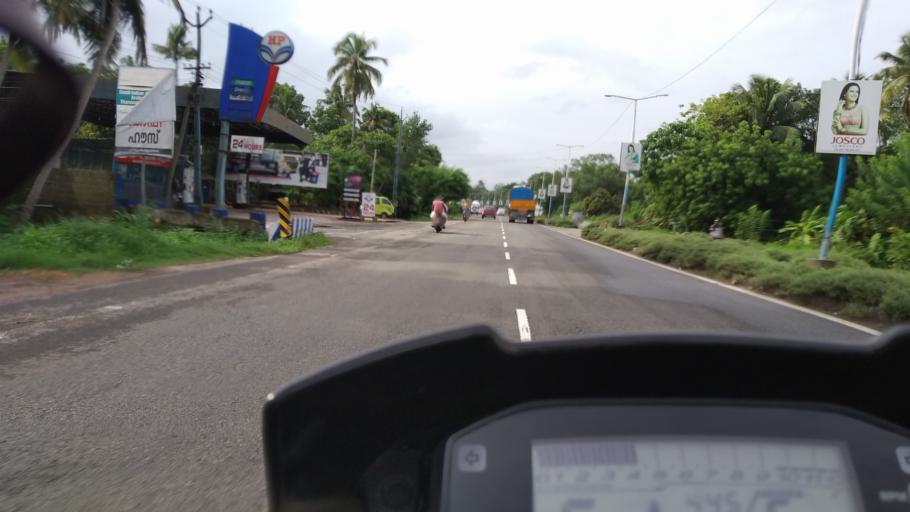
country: IN
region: Kerala
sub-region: Alappuzha
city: Kutiatodu
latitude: 9.7777
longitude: 76.3181
